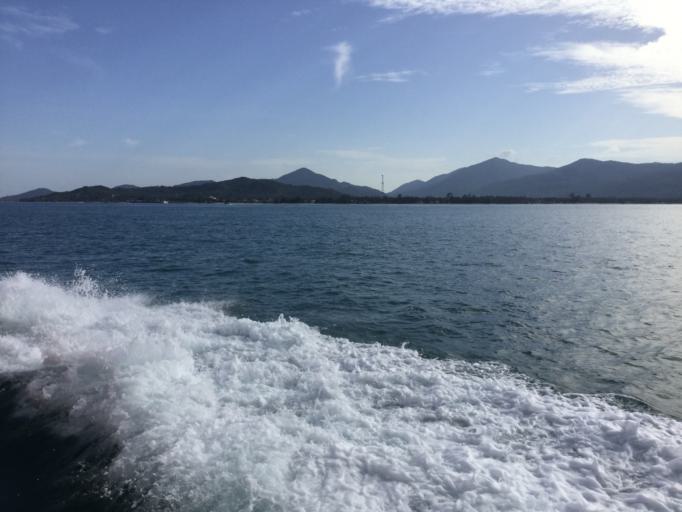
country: TH
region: Surat Thani
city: Ko Pha-Ngan
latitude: 9.6899
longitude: 99.9855
